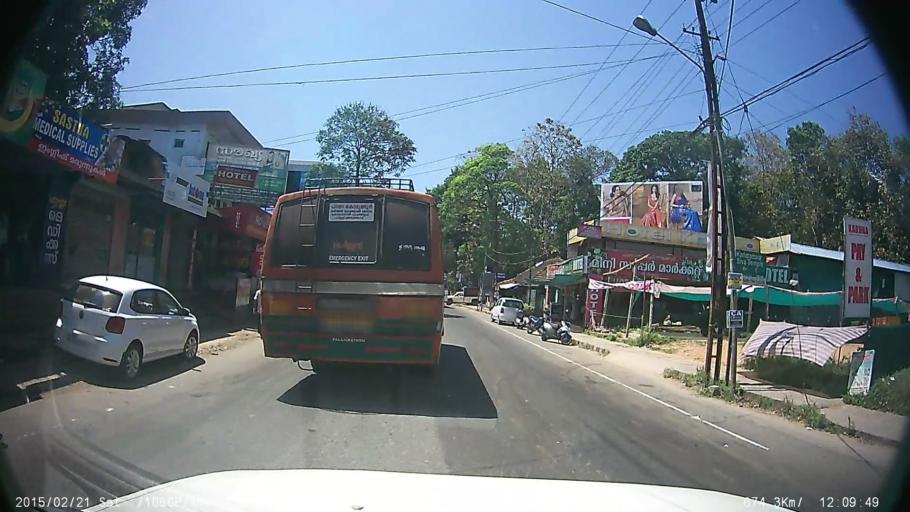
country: IN
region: Kerala
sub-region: Kottayam
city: Lalam
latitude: 9.7083
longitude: 76.6723
